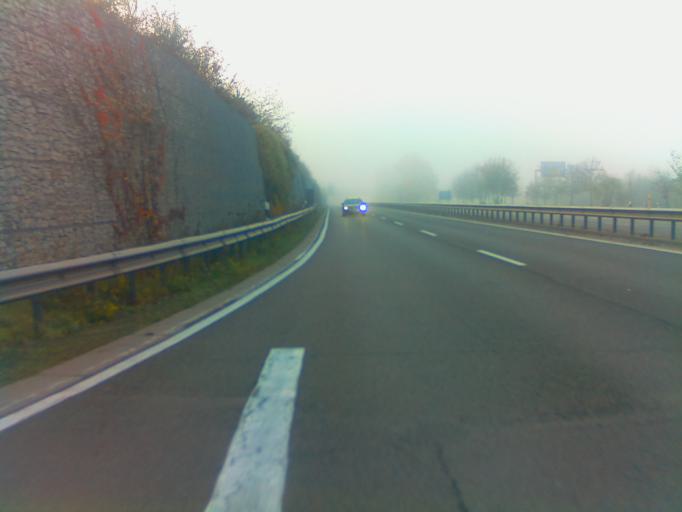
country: DE
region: Rheinland-Pfalz
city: Frankenthal
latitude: 49.4896
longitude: 8.3575
